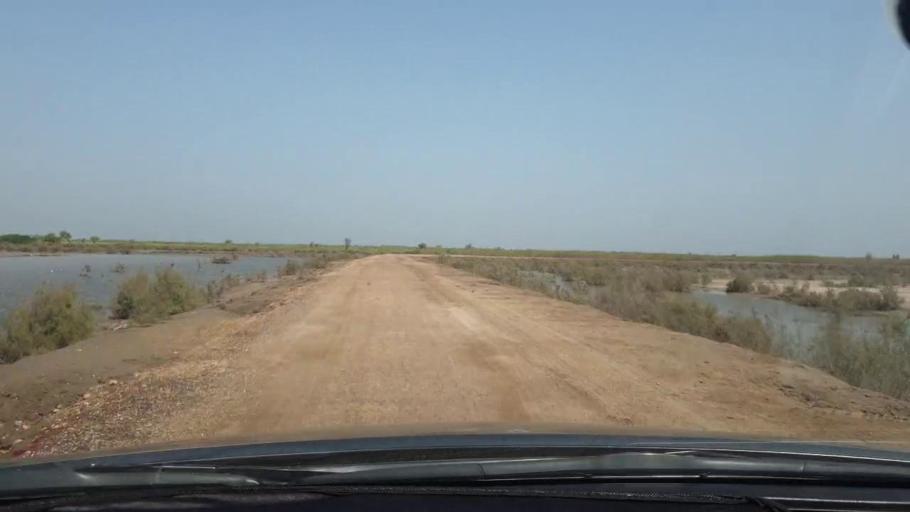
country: PK
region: Sindh
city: Tando Bago
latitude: 24.7907
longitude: 69.0787
